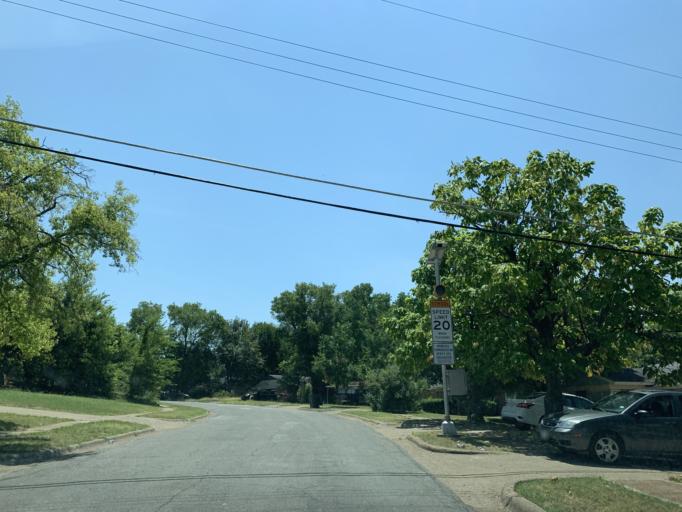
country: US
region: Texas
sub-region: Dallas County
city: Hutchins
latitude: 32.6809
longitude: -96.7643
